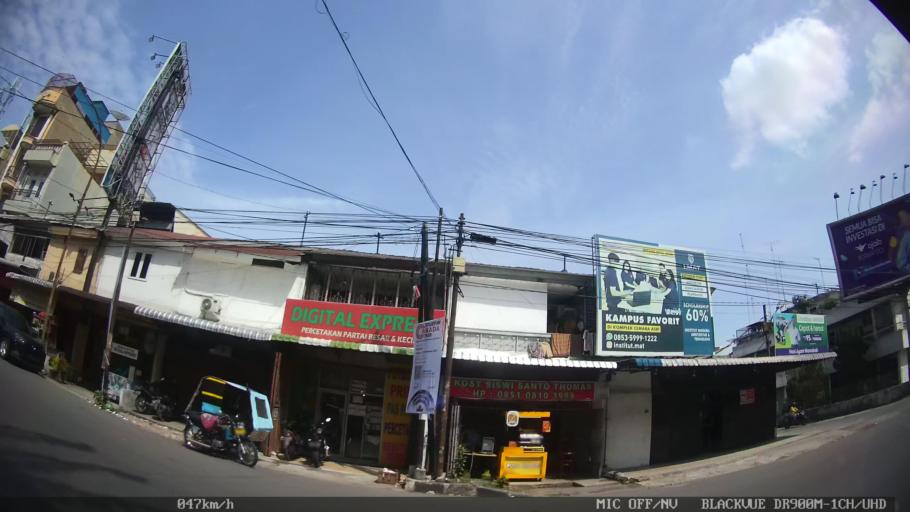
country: ID
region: North Sumatra
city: Medan
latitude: 3.5888
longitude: 98.6680
